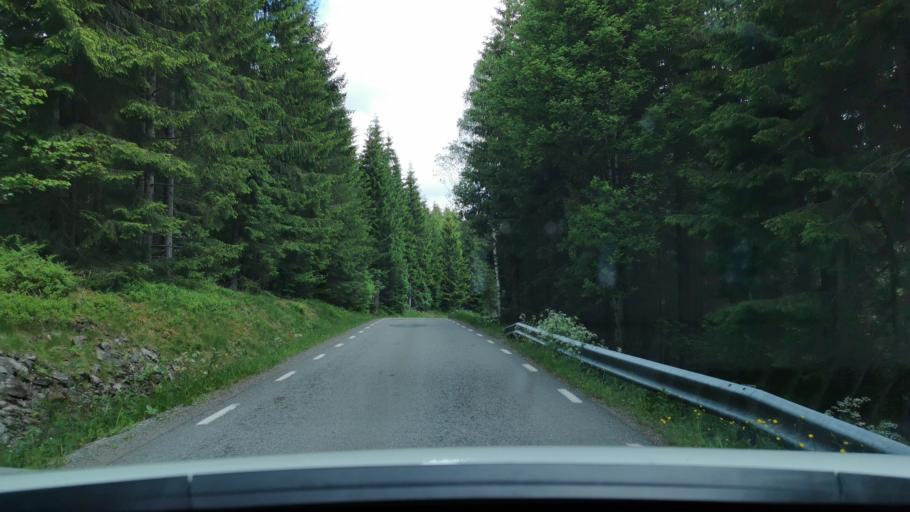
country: SE
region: Vaestra Goetaland
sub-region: Bengtsfors Kommun
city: Dals Langed
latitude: 58.8131
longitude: 12.3258
